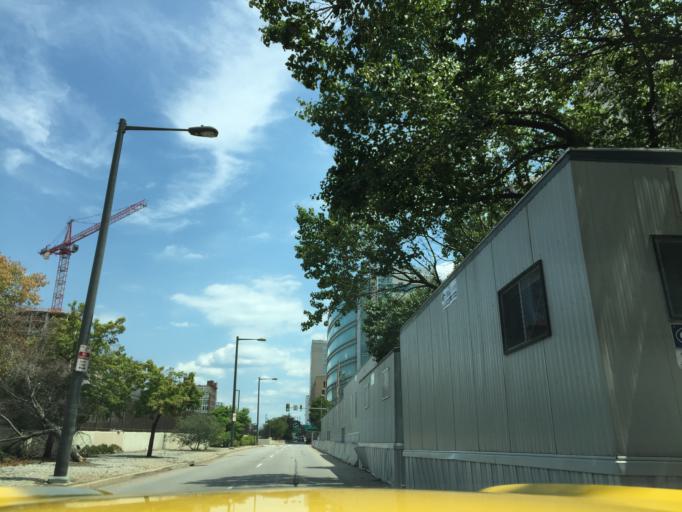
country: US
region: Pennsylvania
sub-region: Philadelphia County
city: Philadelphia
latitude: 39.9584
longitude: -75.1685
